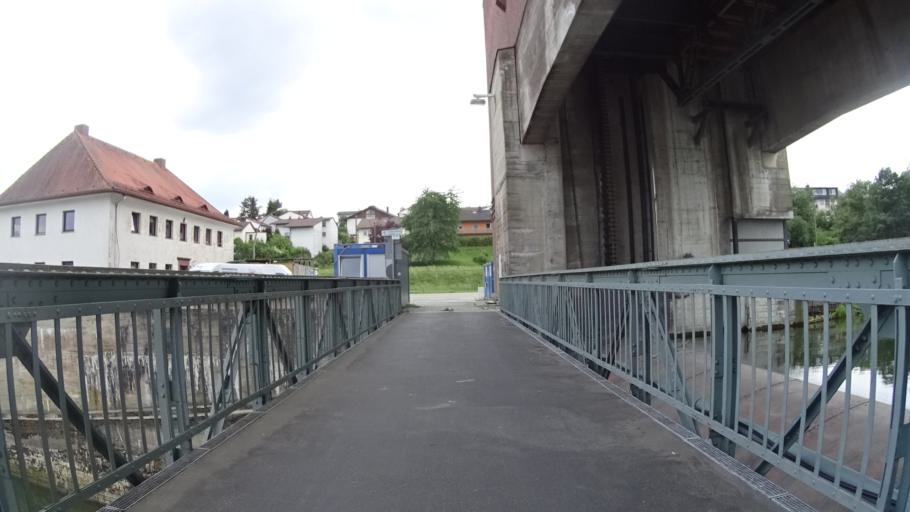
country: DE
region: Bavaria
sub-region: Lower Bavaria
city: Passau
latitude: 48.5777
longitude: 13.4056
